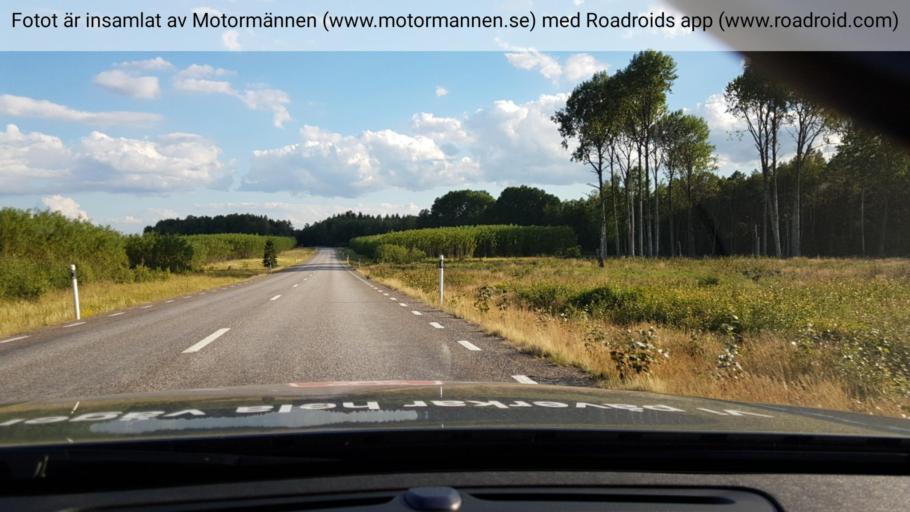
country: SE
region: Uppsala
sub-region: Heby Kommun
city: Morgongava
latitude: 59.8505
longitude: 16.9286
